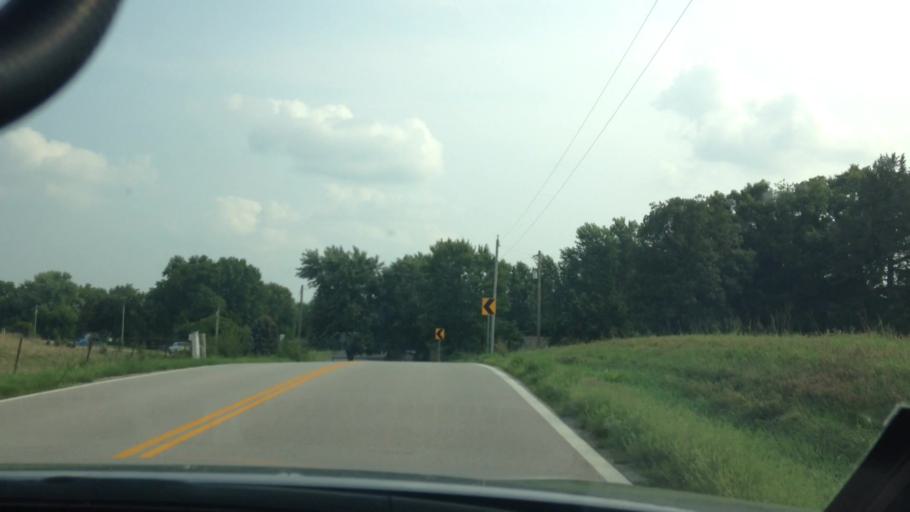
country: US
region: Kansas
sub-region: Leavenworth County
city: Lansing
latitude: 39.2497
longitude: -94.8761
